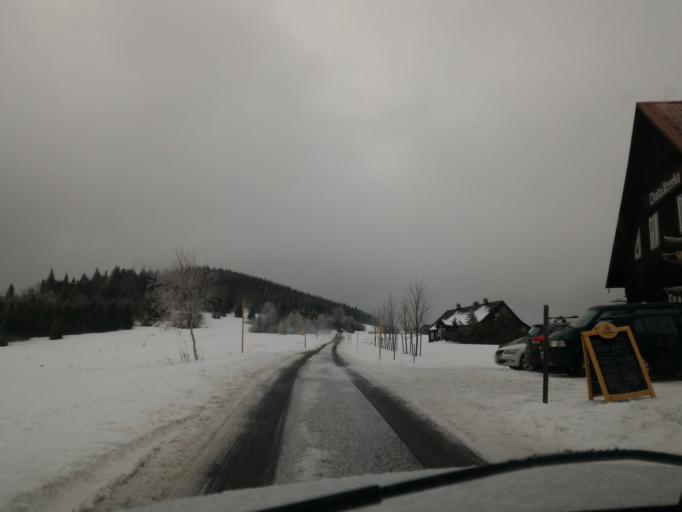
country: CZ
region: Liberecky
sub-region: Okres Jablonec nad Nisou
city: Korenov
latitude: 50.8166
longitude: 15.3482
